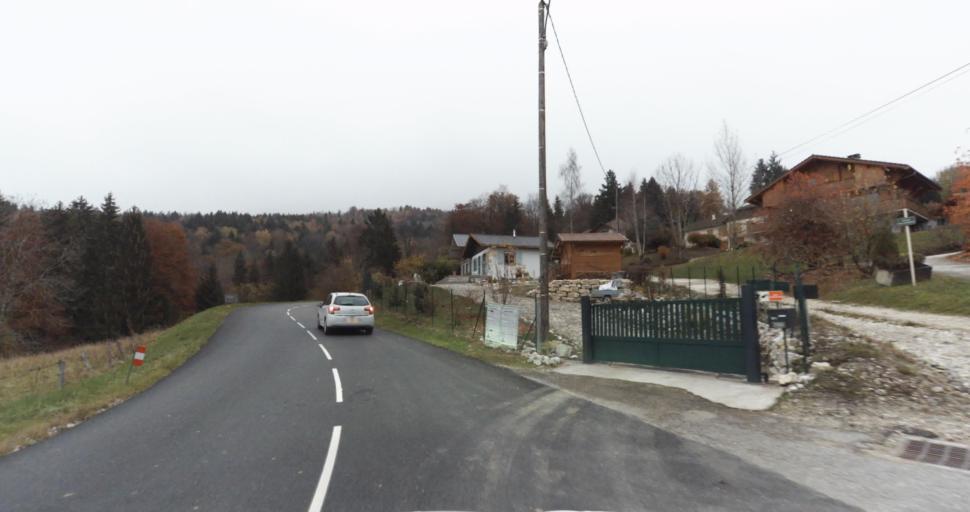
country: FR
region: Rhone-Alpes
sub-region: Departement de la Haute-Savoie
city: Saint-Jorioz
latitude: 45.7926
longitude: 6.1491
